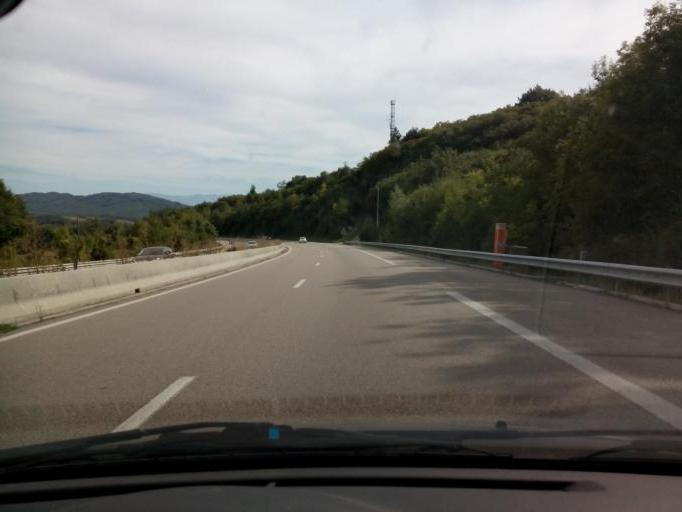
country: FR
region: Rhone-Alpes
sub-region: Departement de l'Isere
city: Chabons
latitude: 45.4483
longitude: 5.3992
